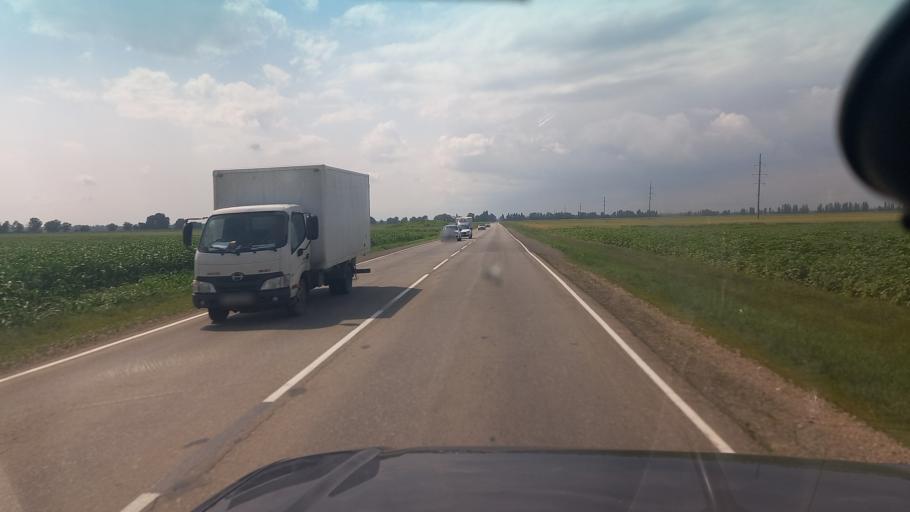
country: RU
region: Adygeya
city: Koshekhabl'
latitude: 44.9049
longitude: 40.4669
